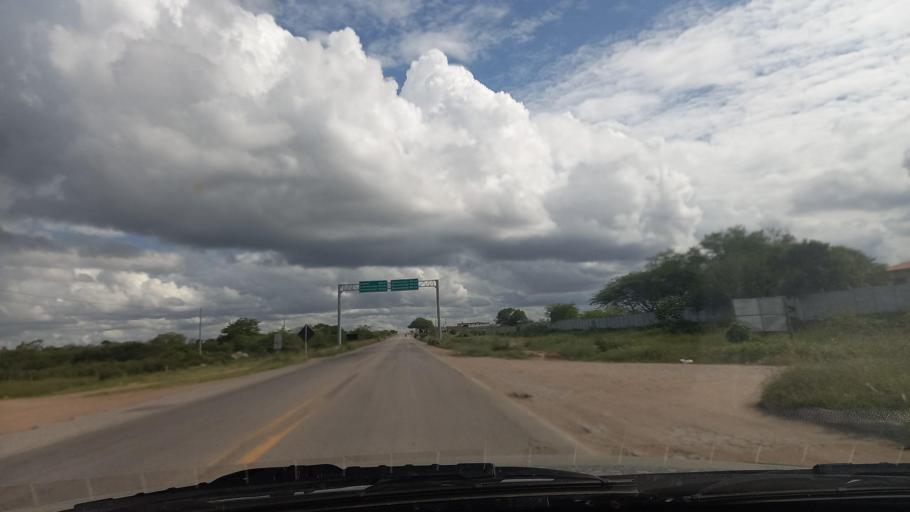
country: BR
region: Pernambuco
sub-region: Cachoeirinha
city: Cachoeirinha
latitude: -8.4942
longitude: -36.2380
